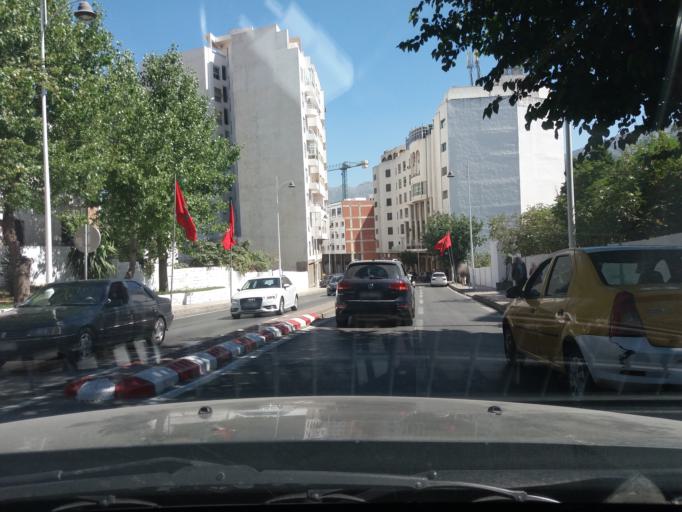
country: MA
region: Tanger-Tetouan
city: Tetouan
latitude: 35.5672
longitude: -5.3711
